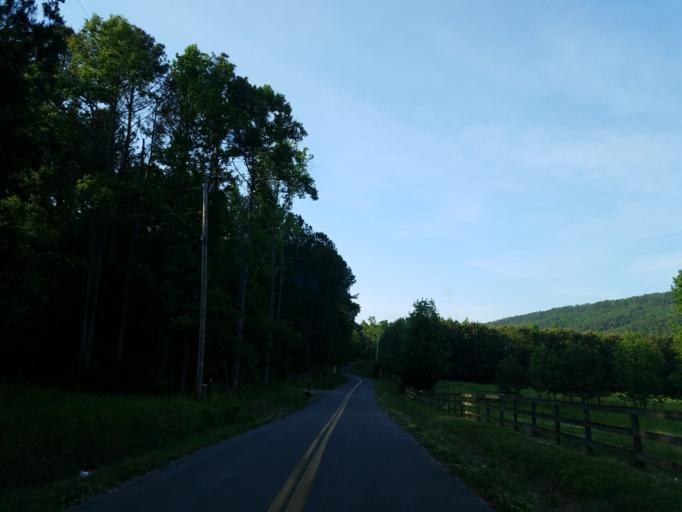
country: US
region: Georgia
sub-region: Gordon County
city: Calhoun
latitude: 34.5543
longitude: -85.1054
